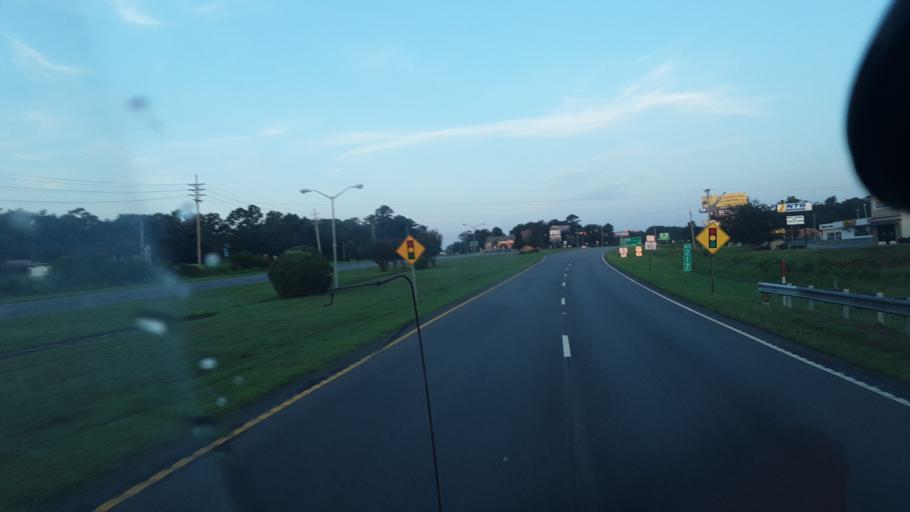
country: US
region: South Carolina
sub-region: Horry County
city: Little River
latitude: 33.8657
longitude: -78.6417
